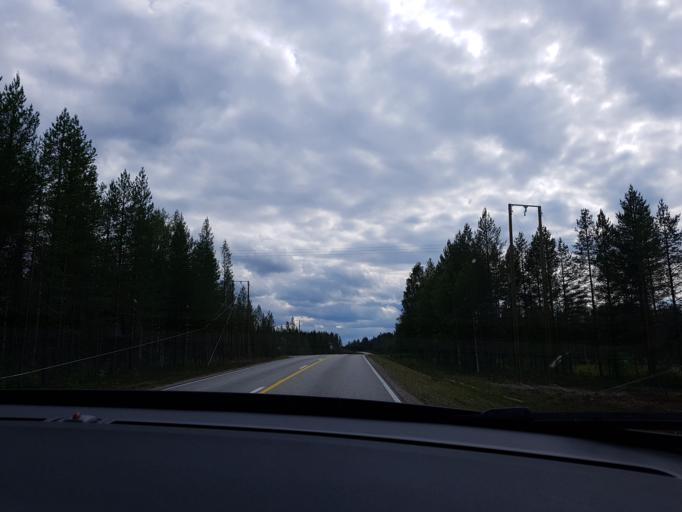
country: FI
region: Kainuu
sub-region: Kehys-Kainuu
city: Kuhmo
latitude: 64.3303
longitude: 29.8757
